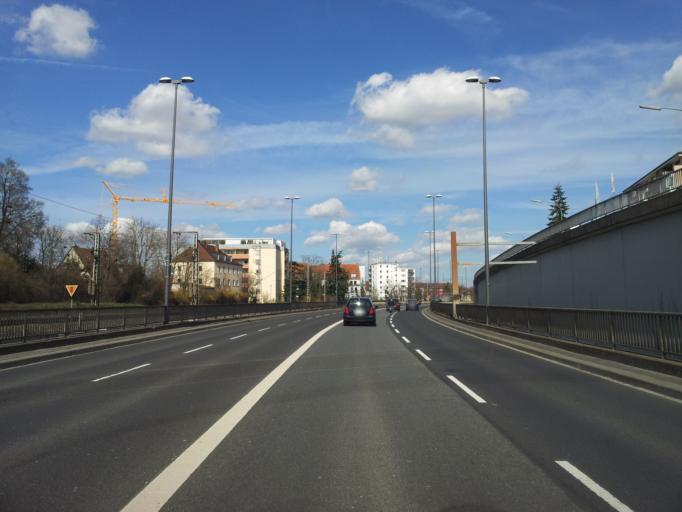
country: DE
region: Bavaria
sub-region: Regierungsbezirk Unterfranken
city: Wuerzburg
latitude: 49.7859
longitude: 9.9413
